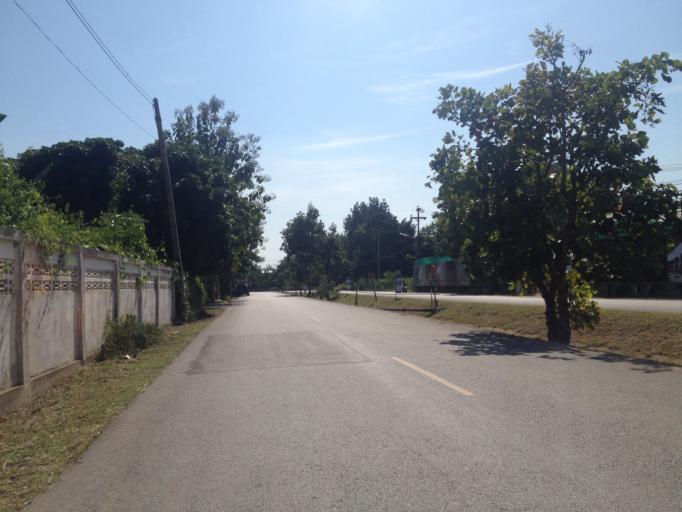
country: TH
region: Chiang Mai
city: Hang Dong
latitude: 18.6967
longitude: 98.9257
